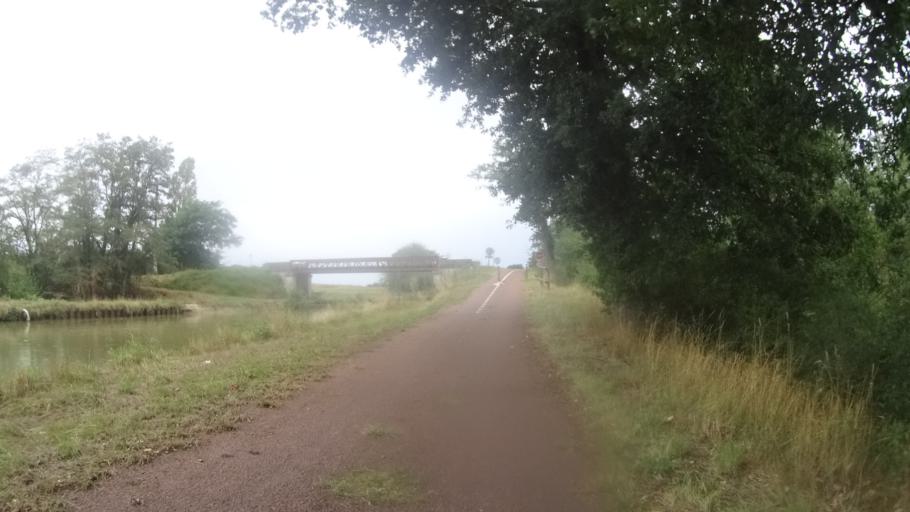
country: FR
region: Bourgogne
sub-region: Departement de la Nievre
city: Imphy
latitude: 46.8571
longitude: 3.2917
